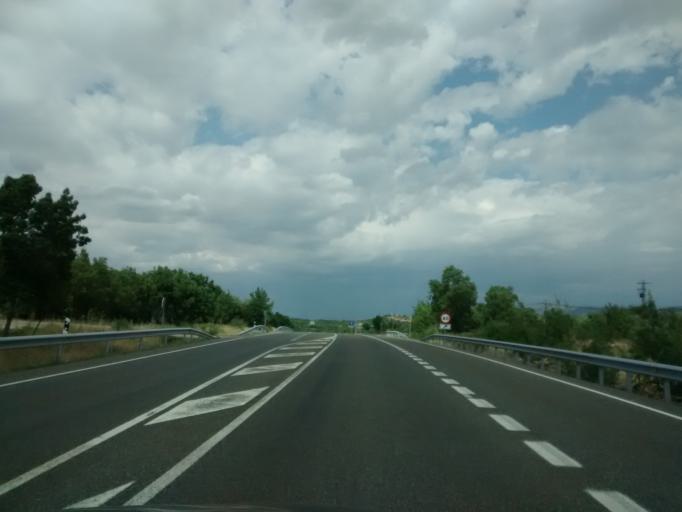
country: ES
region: Castille and Leon
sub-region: Provincia de Segovia
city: Navafria
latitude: 41.0681
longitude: -3.8161
